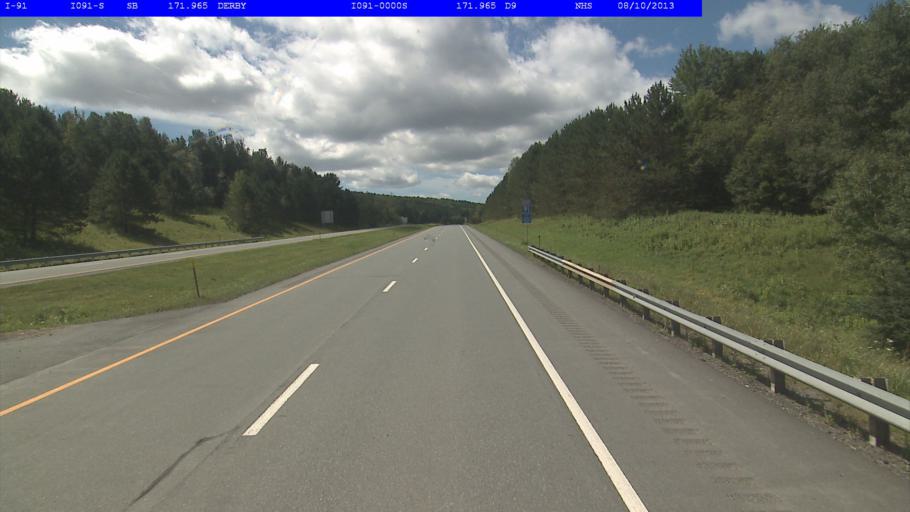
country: US
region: Vermont
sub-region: Orleans County
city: Newport
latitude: 44.9468
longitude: -72.1551
